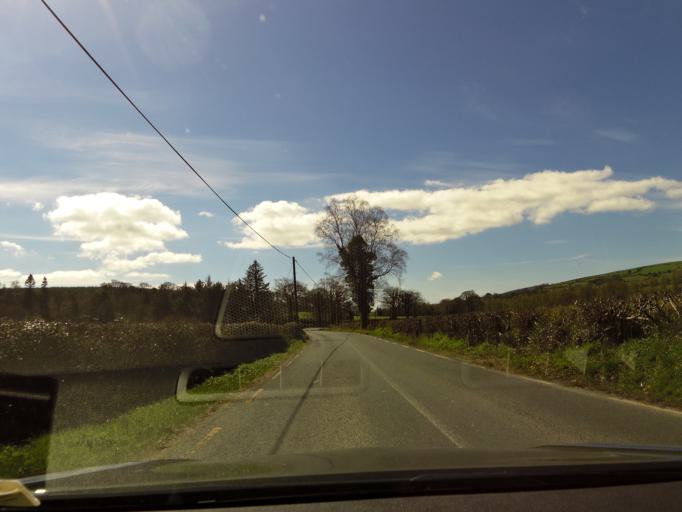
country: IE
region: Leinster
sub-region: Wicklow
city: Aughrim
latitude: 52.8081
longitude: -6.4171
